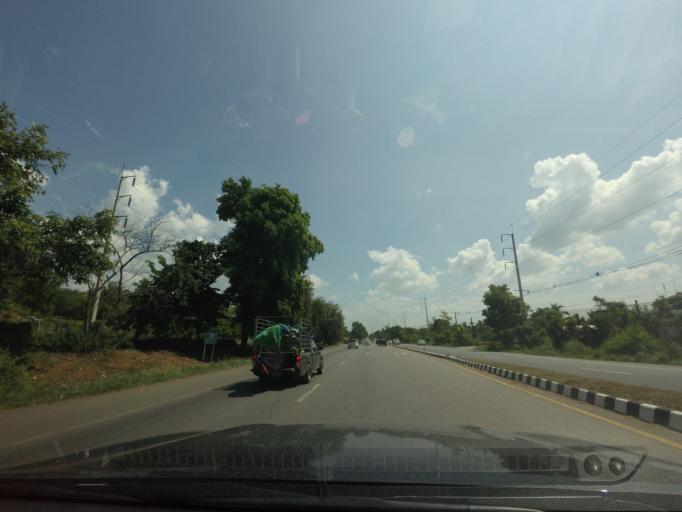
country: TH
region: Phetchabun
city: Nong Phai
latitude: 16.0700
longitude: 101.0688
